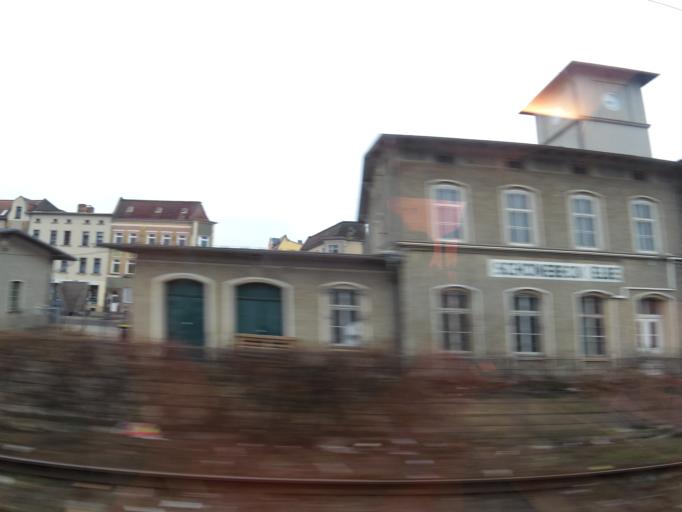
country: DE
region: Saxony-Anhalt
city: Schonebeck
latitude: 52.0184
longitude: 11.7338
